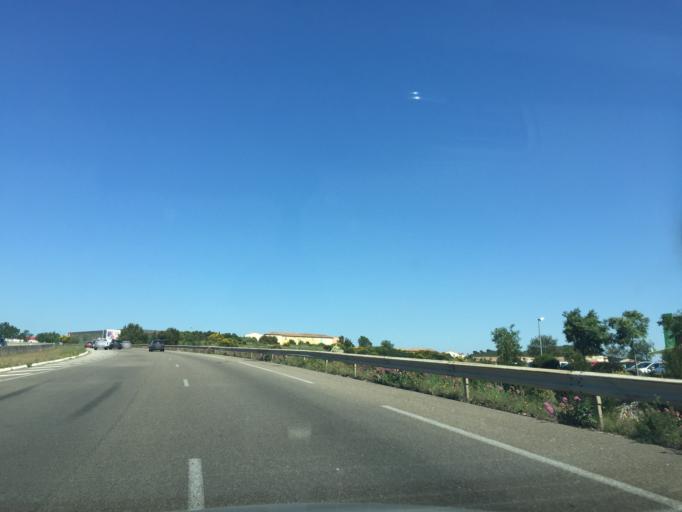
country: FR
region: Languedoc-Roussillon
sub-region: Departement du Gard
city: Les Angles
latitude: 43.9568
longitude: 4.7545
